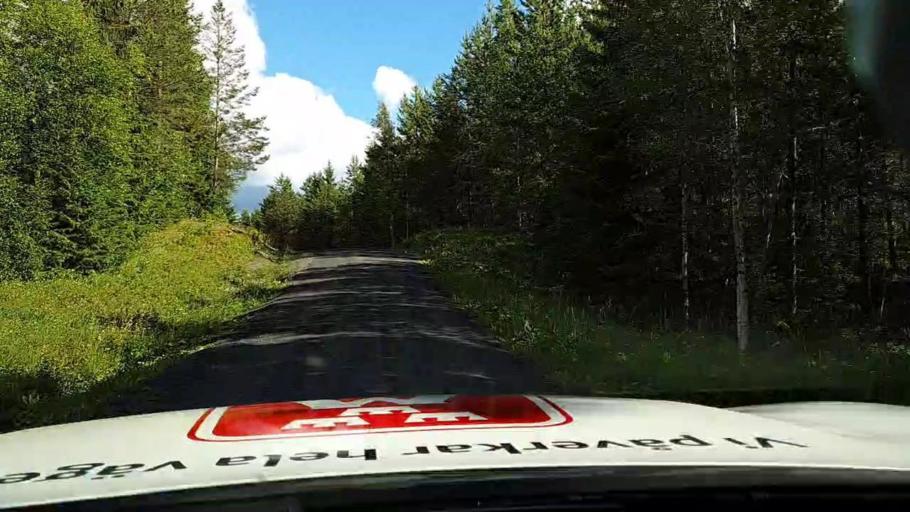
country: SE
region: Jaemtland
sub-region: Krokoms Kommun
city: Valla
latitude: 63.3242
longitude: 13.7474
